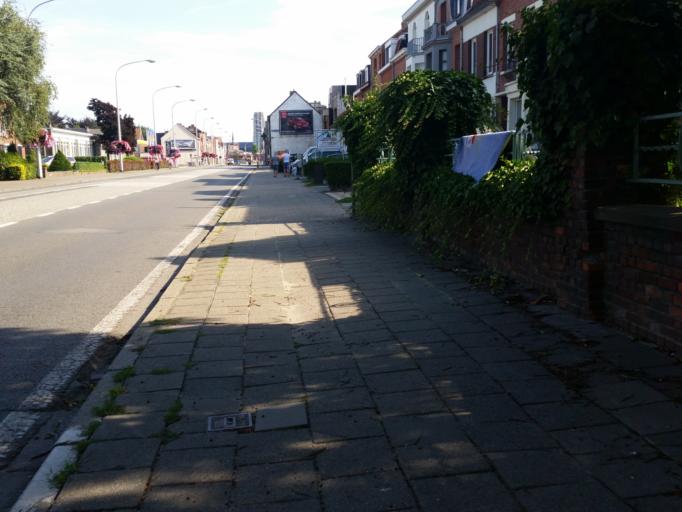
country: BE
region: Flanders
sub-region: Provincie Antwerpen
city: Mechelen
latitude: 51.0416
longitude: 4.4711
